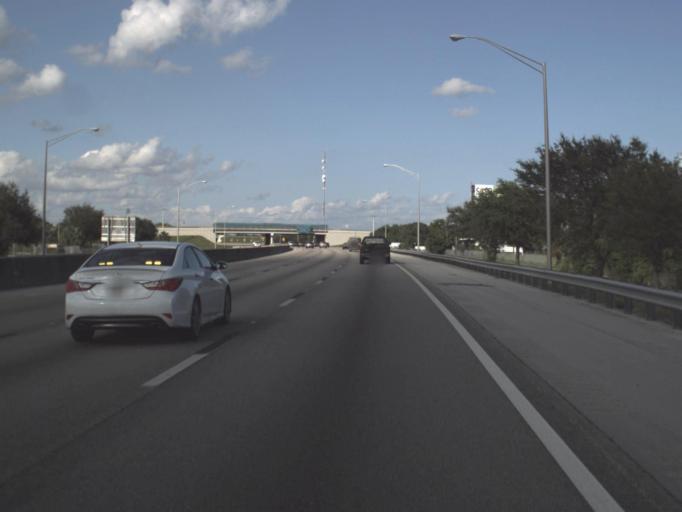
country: US
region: Florida
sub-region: Broward County
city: Coconut Creek
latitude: 26.2415
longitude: -80.1692
